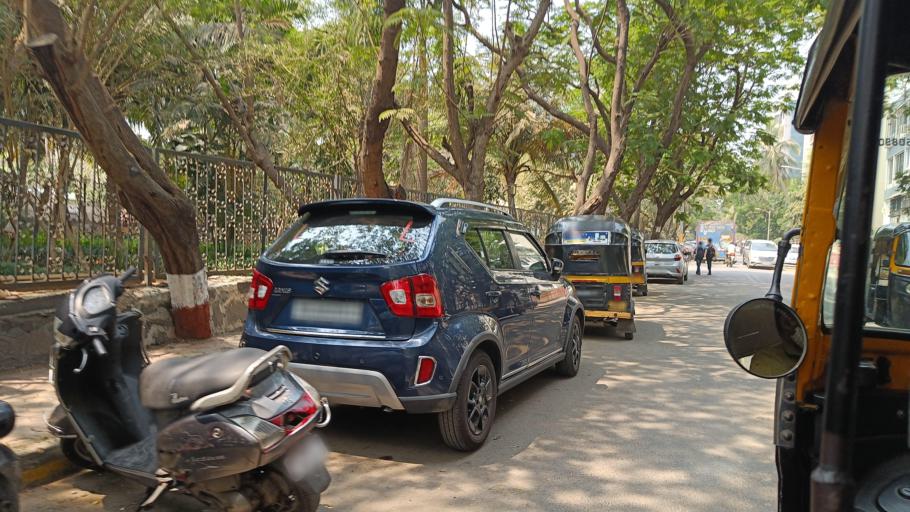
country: IN
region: Maharashtra
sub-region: Mumbai Suburban
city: Mumbai
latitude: 19.1118
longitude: 72.8319
